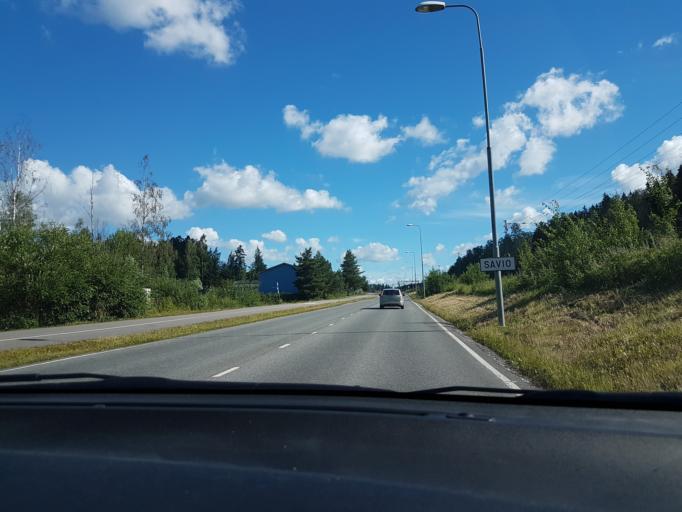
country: FI
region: Uusimaa
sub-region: Helsinki
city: Kerava
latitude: 60.3672
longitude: 25.0897
